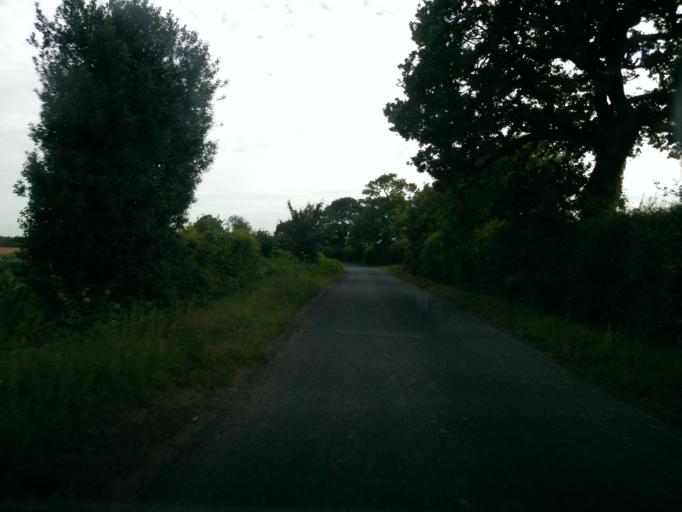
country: GB
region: England
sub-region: Essex
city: Great Bentley
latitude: 51.8382
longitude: 1.0838
